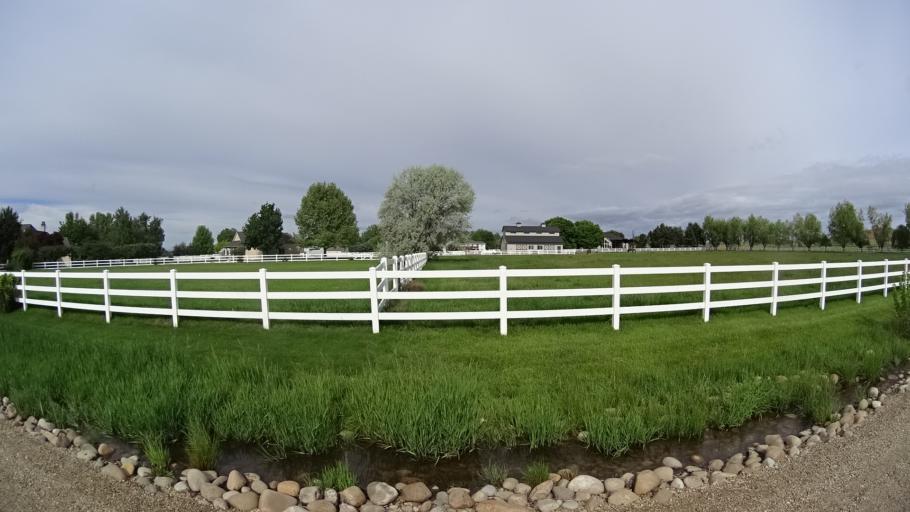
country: US
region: Idaho
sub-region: Ada County
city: Eagle
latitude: 43.7307
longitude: -116.4034
